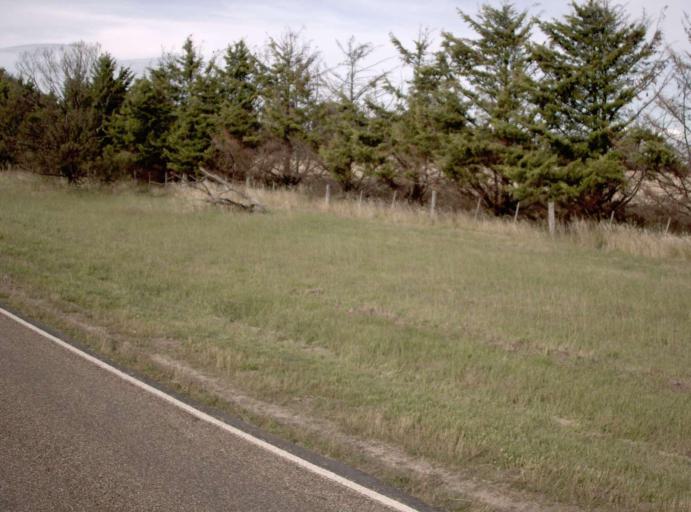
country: AU
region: Victoria
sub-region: Wellington
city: Heyfield
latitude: -38.0355
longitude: 146.6669
